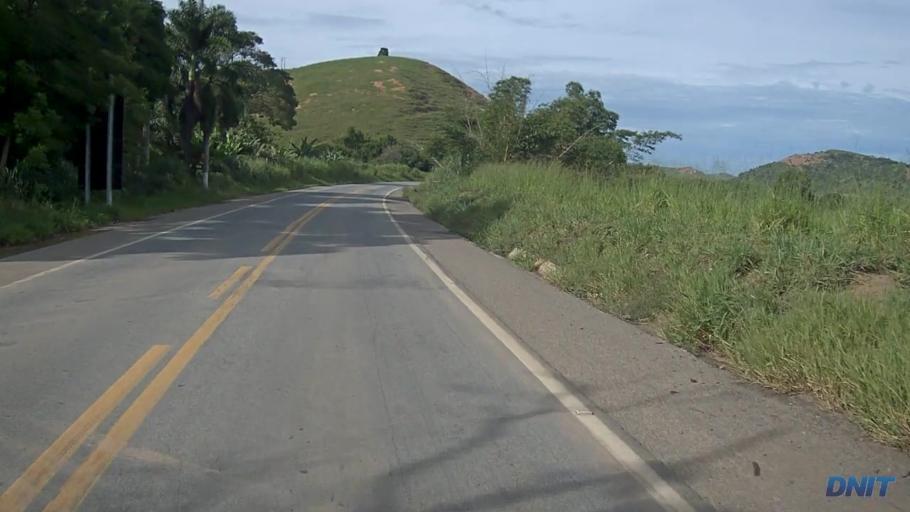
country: BR
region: Minas Gerais
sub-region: Belo Oriente
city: Belo Oriente
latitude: -19.1668
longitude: -42.2457
